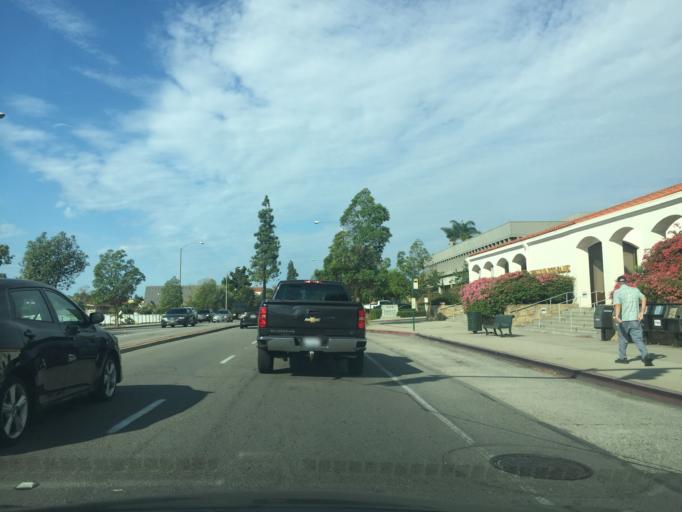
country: US
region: California
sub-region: Santa Barbara County
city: Mission Canyon
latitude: 34.4406
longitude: -119.7468
